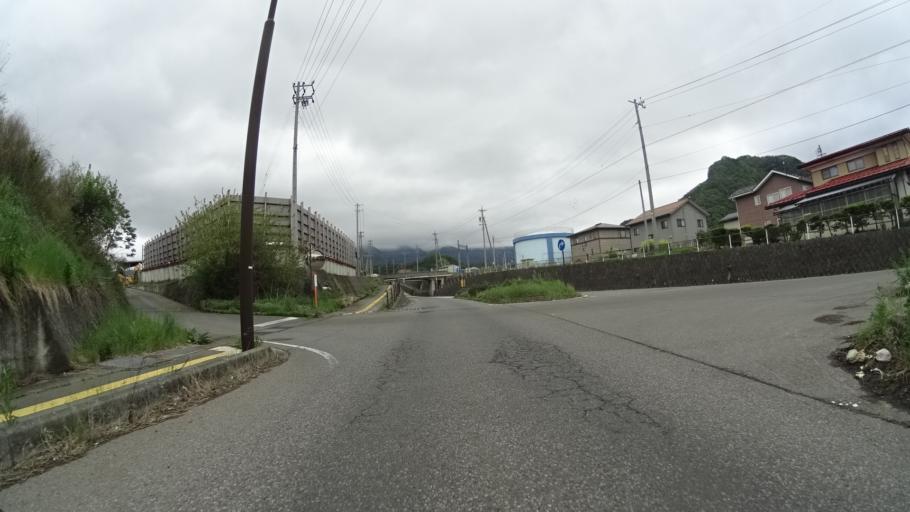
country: JP
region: Nagano
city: Nakano
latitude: 36.7586
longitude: 138.3844
